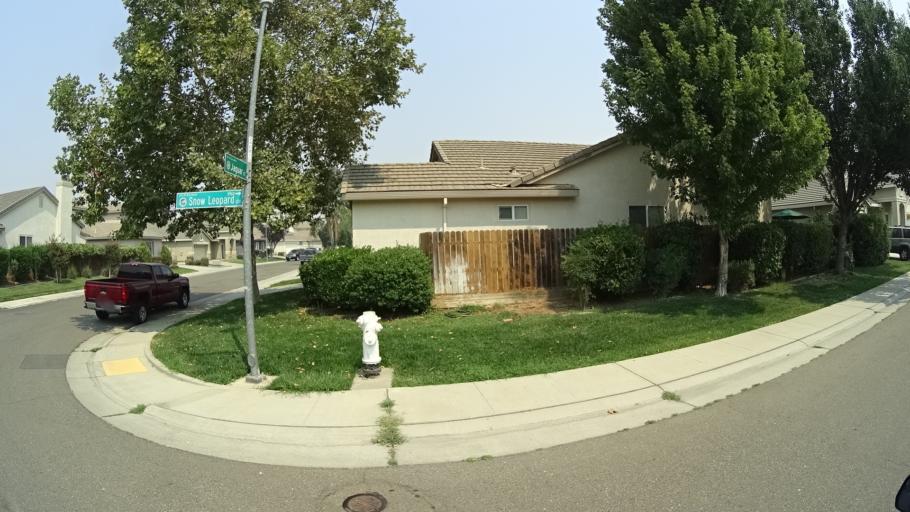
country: US
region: California
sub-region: Sacramento County
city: Laguna
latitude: 38.4017
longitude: -121.4325
